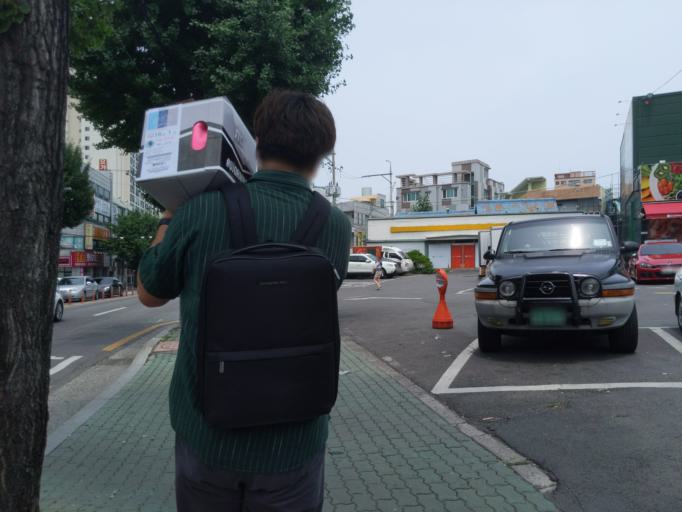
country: KR
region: Daegu
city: Hwawon
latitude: 35.8110
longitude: 128.5259
